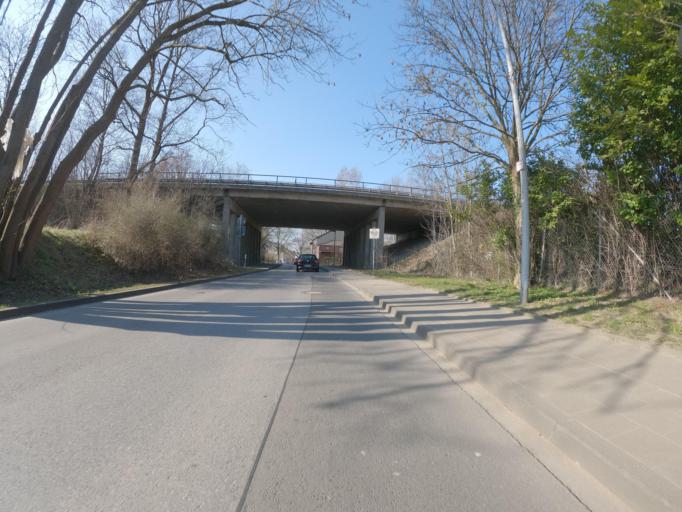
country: DE
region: North Rhine-Westphalia
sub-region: Regierungsbezirk Koln
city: Wurselen
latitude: 50.7897
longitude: 6.1327
